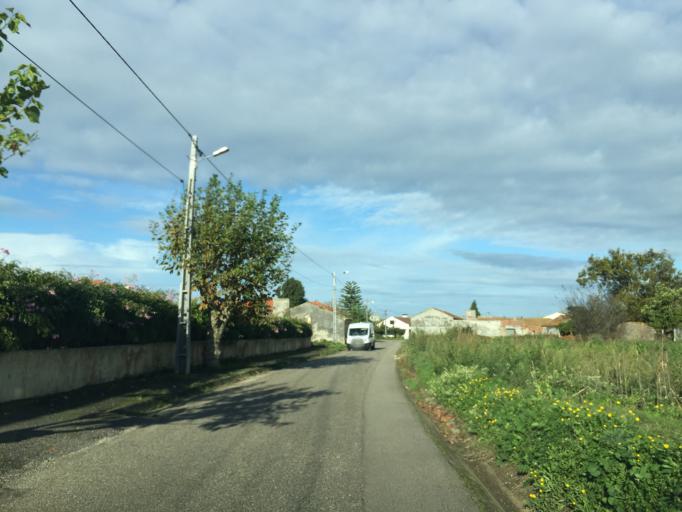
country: PT
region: Coimbra
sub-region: Figueira da Foz
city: Lavos
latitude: 40.0641
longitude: -8.8180
